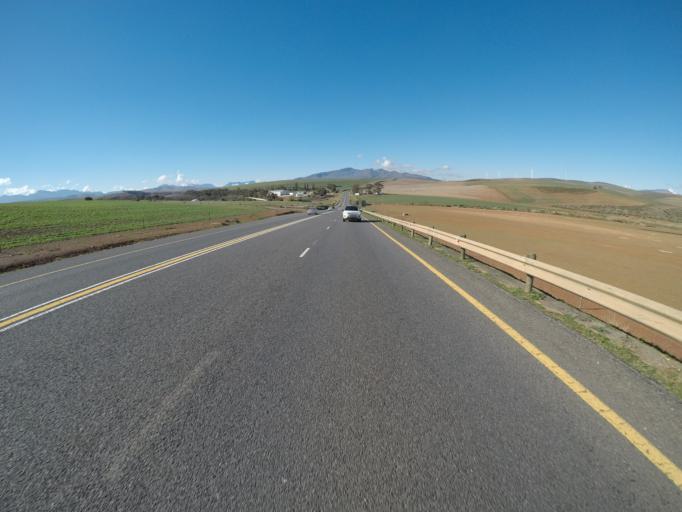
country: ZA
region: Western Cape
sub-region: Overberg District Municipality
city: Caledon
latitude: -34.2119
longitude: 19.3331
